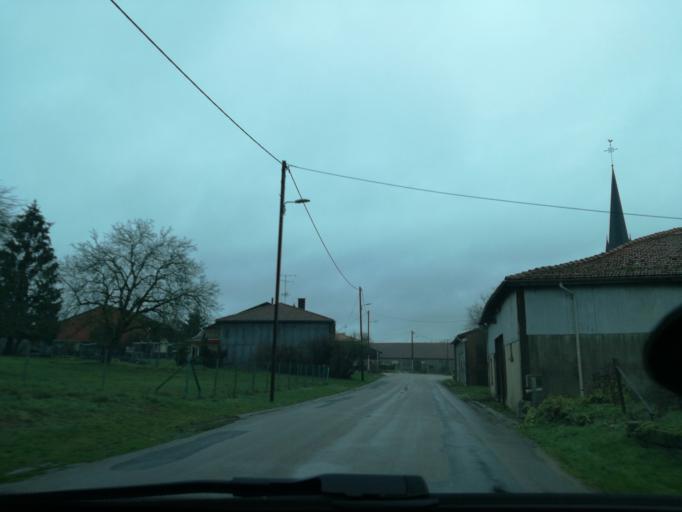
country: FR
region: Lorraine
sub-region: Departement de la Meuse
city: Clermont-en-Argonne
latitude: 49.0191
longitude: 5.1058
